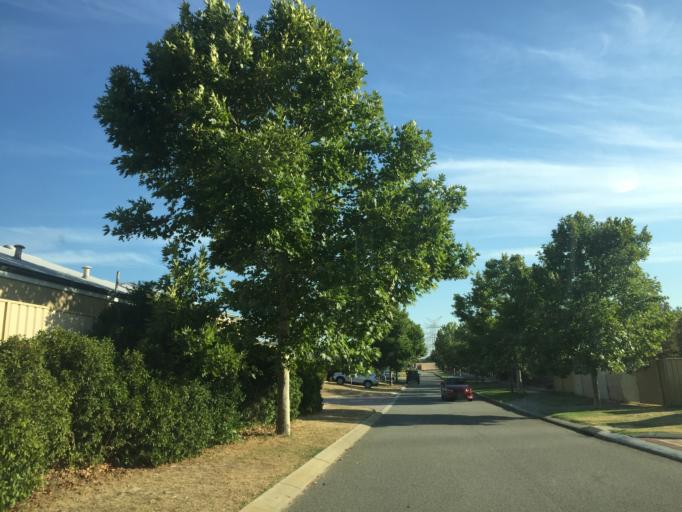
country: AU
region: Western Australia
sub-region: City of Cockburn
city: City of Cockburn
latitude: -32.0931
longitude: 115.8411
